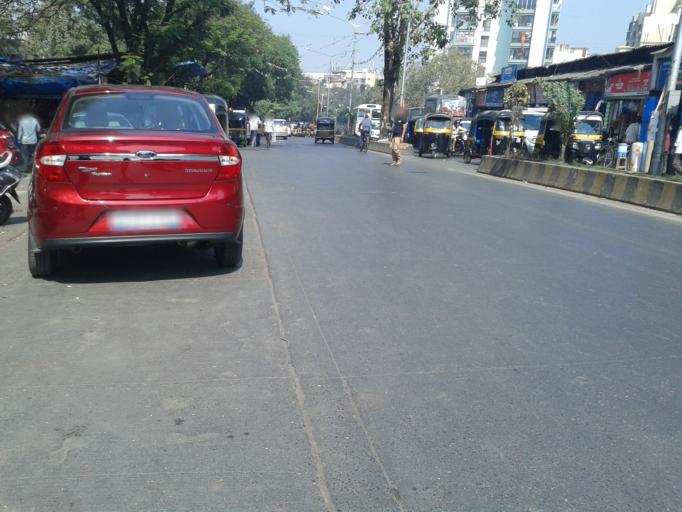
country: IN
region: Maharashtra
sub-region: Mumbai Suburban
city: Borivli
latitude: 19.2512
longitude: 72.8635
